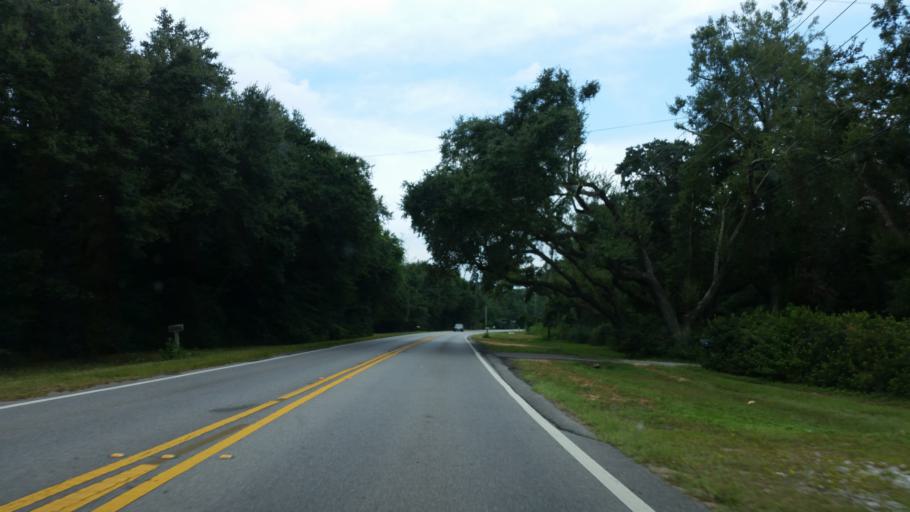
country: US
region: Florida
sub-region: Santa Rosa County
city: Pace
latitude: 30.6240
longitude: -87.1634
